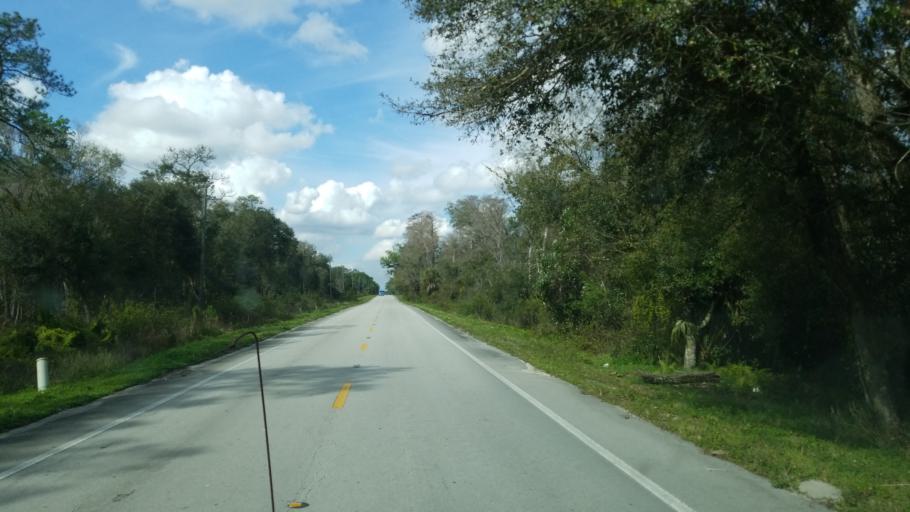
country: US
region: Florida
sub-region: Brevard County
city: June Park
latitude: 27.9781
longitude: -81.0110
